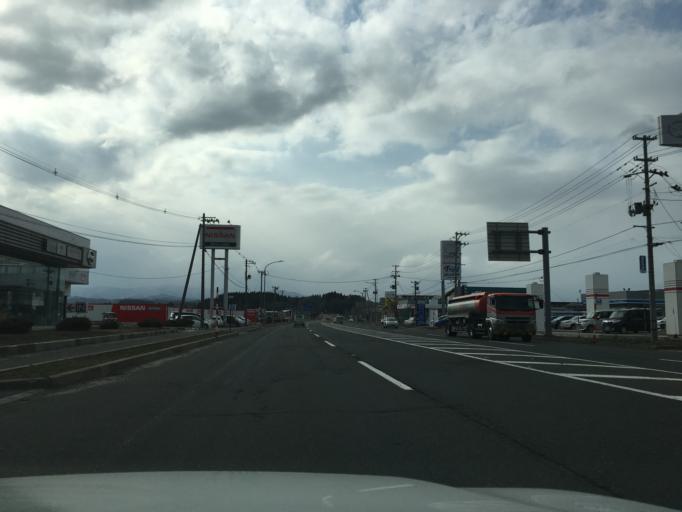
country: JP
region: Aomori
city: Aomori Shi
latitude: 40.8338
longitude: 140.6873
